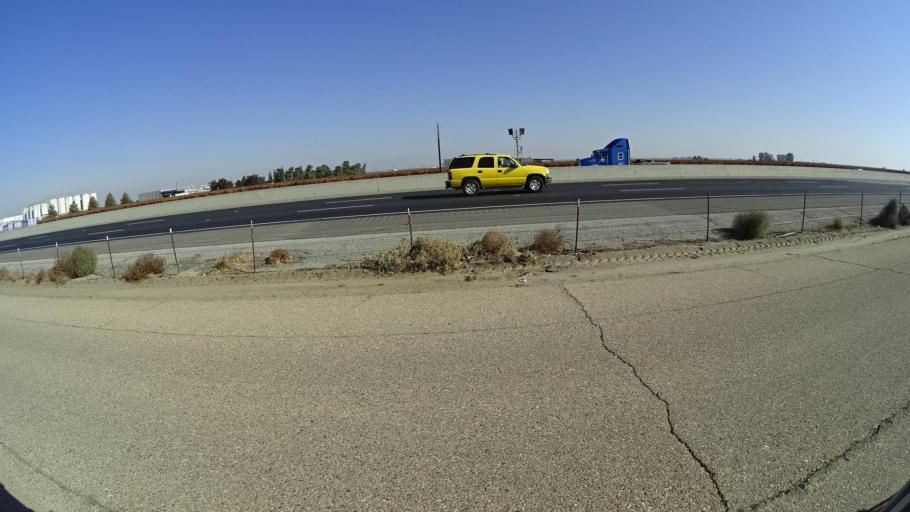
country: US
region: California
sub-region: Kern County
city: McFarland
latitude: 35.7012
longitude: -119.2333
